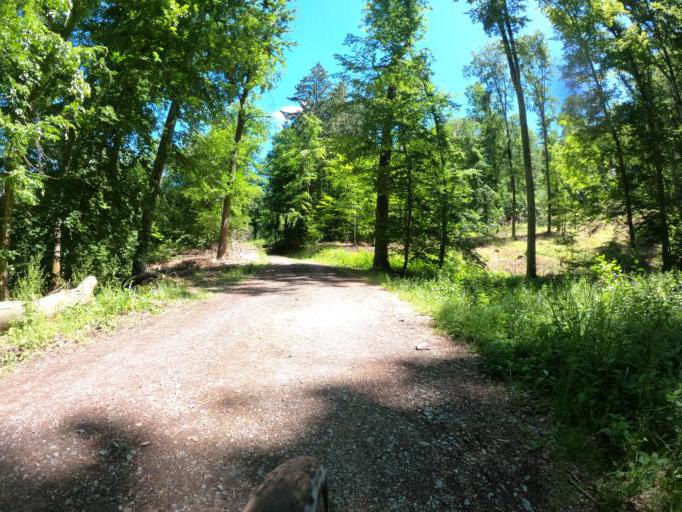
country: DE
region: Baden-Wuerttemberg
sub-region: Regierungsbezirk Stuttgart
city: Pfaffenhofen
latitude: 49.0103
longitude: 8.9795
